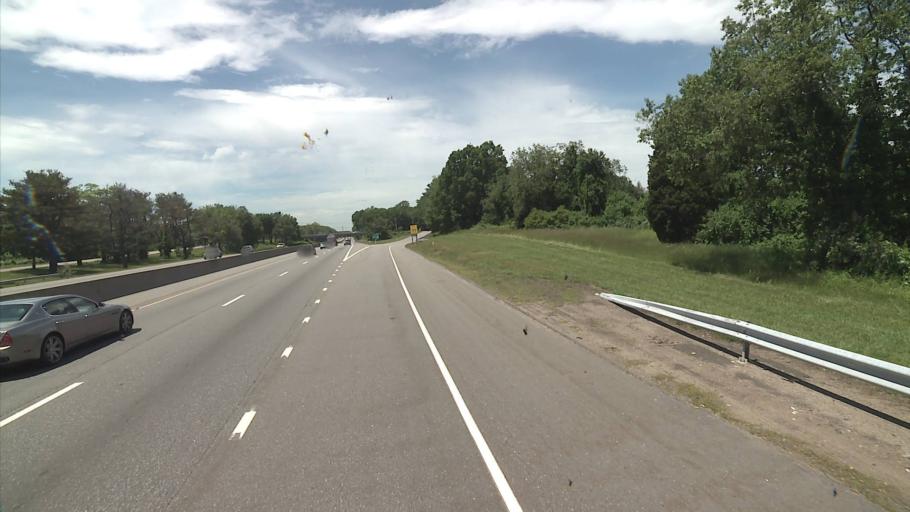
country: US
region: Connecticut
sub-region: New Haven County
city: Madison Center
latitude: 41.2884
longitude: -72.6225
